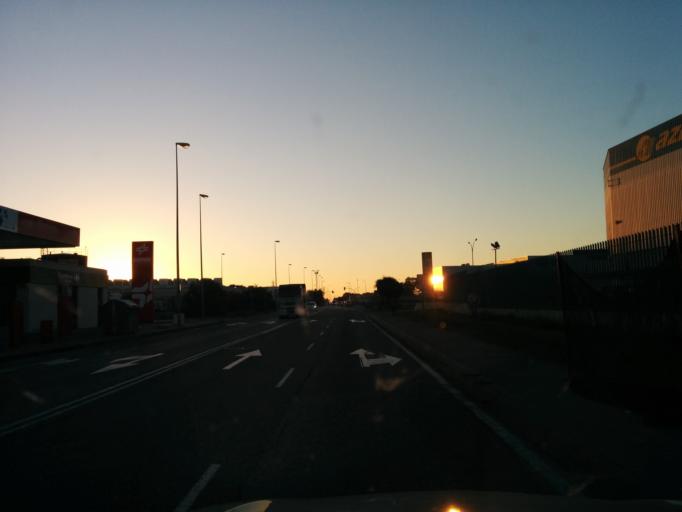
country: ES
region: Andalusia
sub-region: Provincia de Sevilla
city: Sevilla
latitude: 37.3810
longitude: -5.9381
